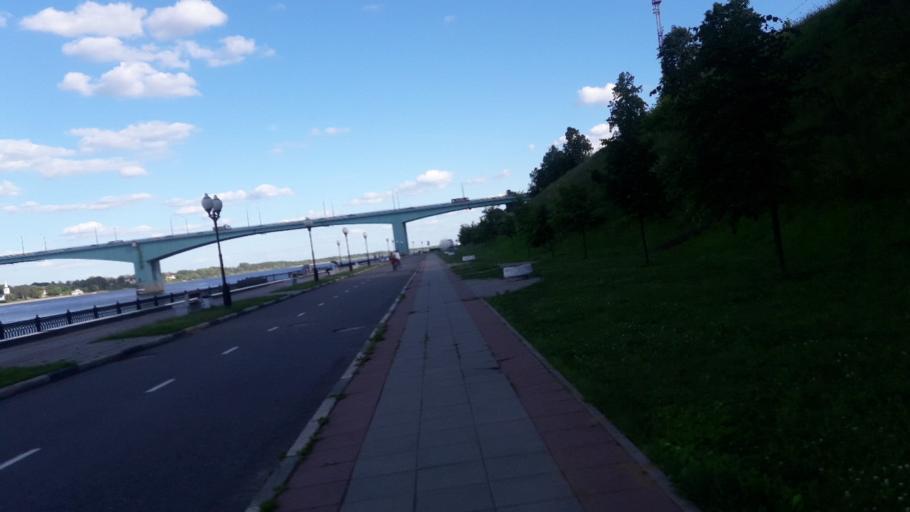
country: RU
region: Jaroslavl
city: Yaroslavl
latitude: 57.6425
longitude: 39.8860
